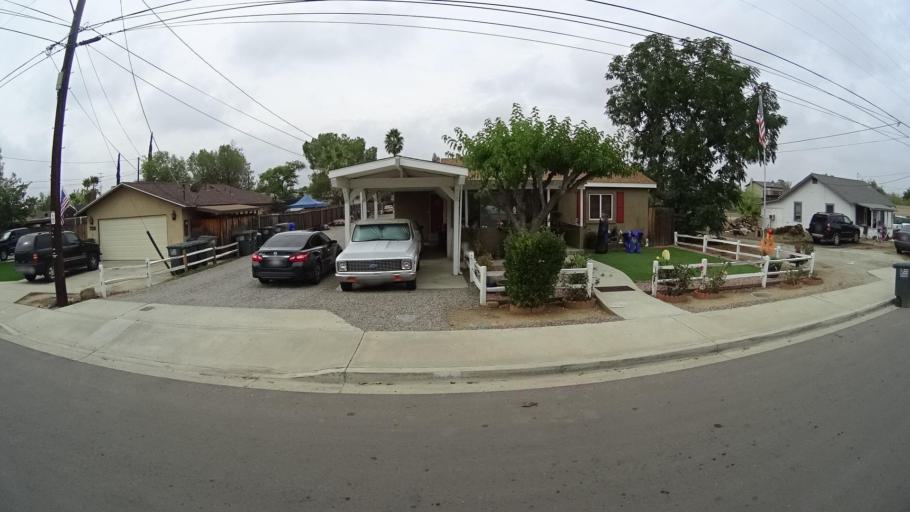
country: US
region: California
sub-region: San Diego County
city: Ramona
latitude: 33.0366
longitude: -116.8689
